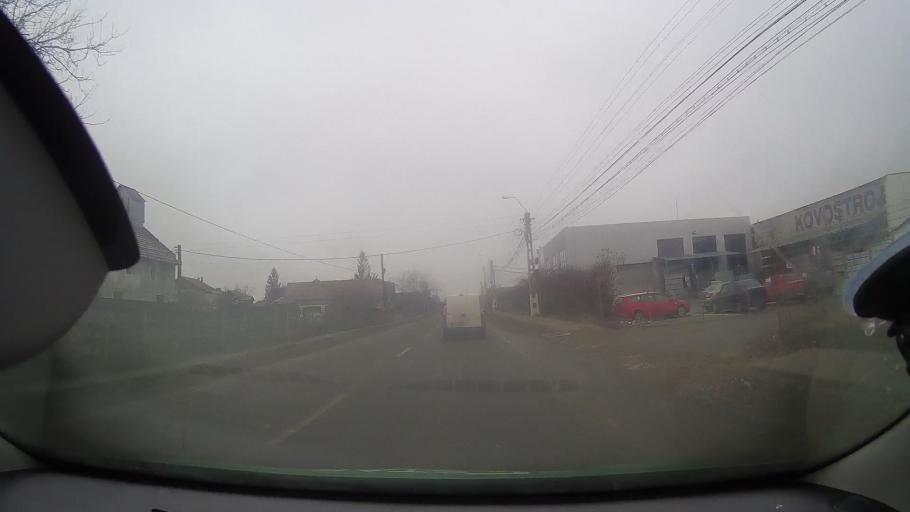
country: RO
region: Cluj
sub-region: Comuna Mihai Viteazu
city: Mihai Viteazu
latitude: 46.5407
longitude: 23.7670
